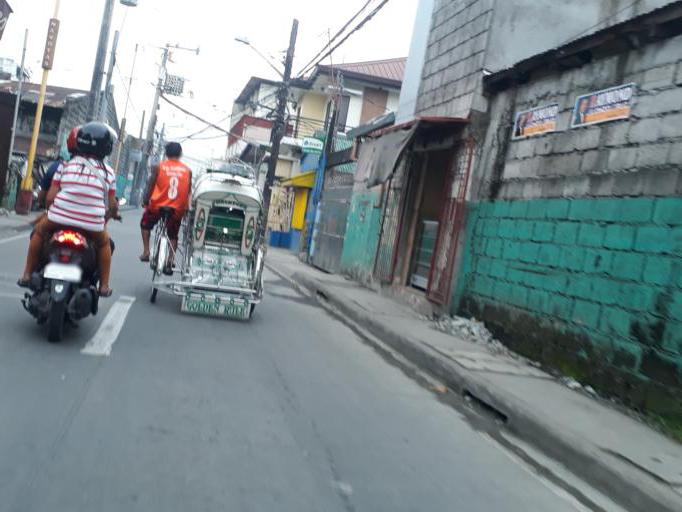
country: PH
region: Calabarzon
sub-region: Province of Rizal
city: Navotas
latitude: 14.6602
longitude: 120.9446
